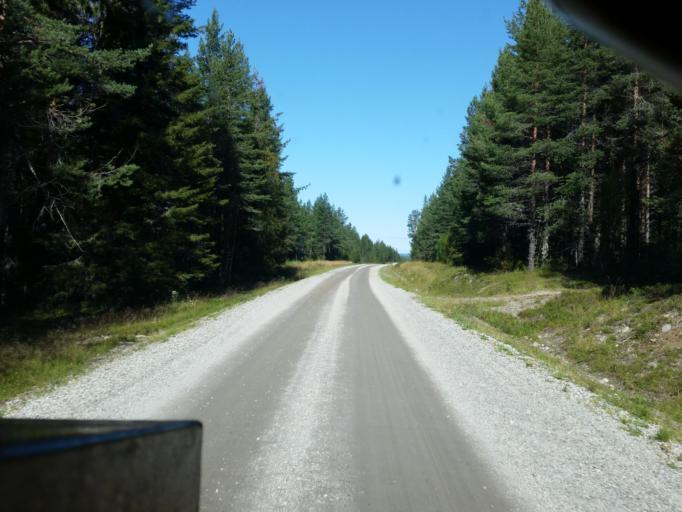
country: SE
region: Vaesterbotten
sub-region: Skelleftea Kommun
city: Storvik
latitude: 65.3102
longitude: 20.6298
